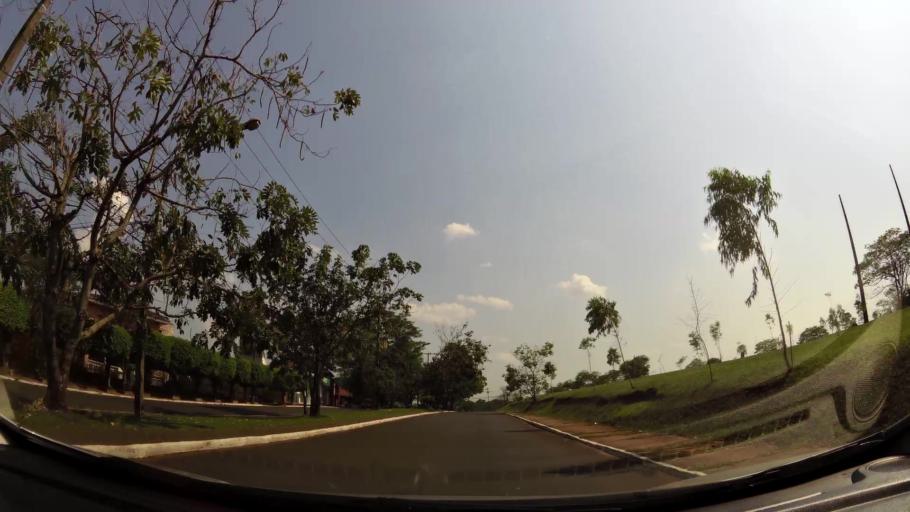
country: PY
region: Alto Parana
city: Ciudad del Este
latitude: -25.5118
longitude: -54.6301
